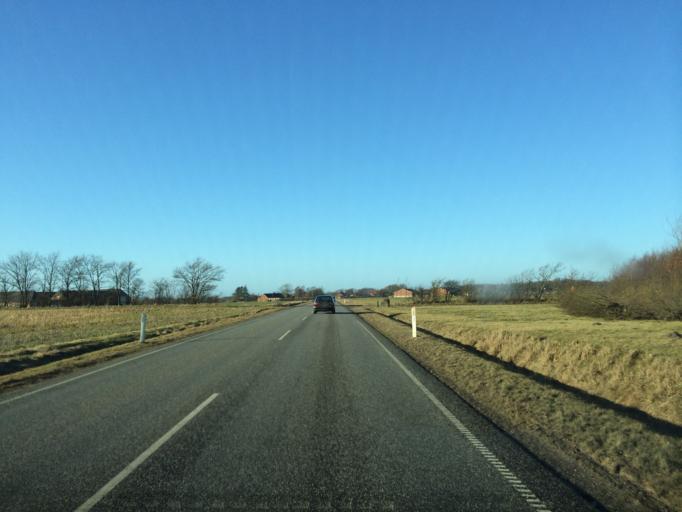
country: DK
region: Central Jutland
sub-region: Ringkobing-Skjern Kommune
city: Ringkobing
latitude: 56.1049
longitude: 8.3250
